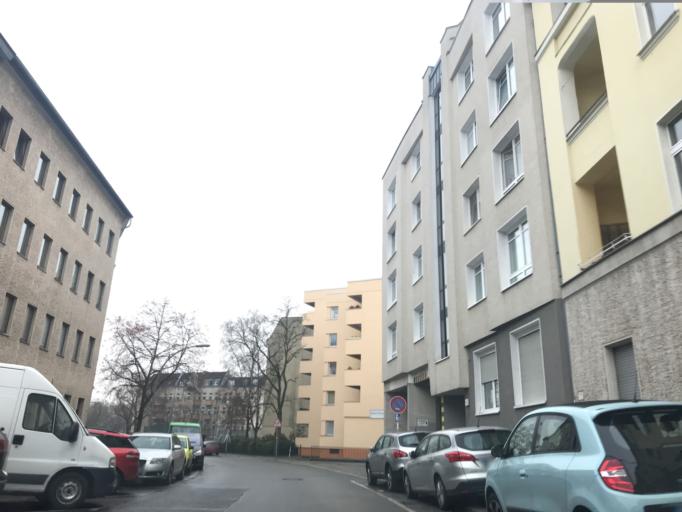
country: DE
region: Berlin
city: Wilhelmstadt
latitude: 52.5251
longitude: 13.1991
